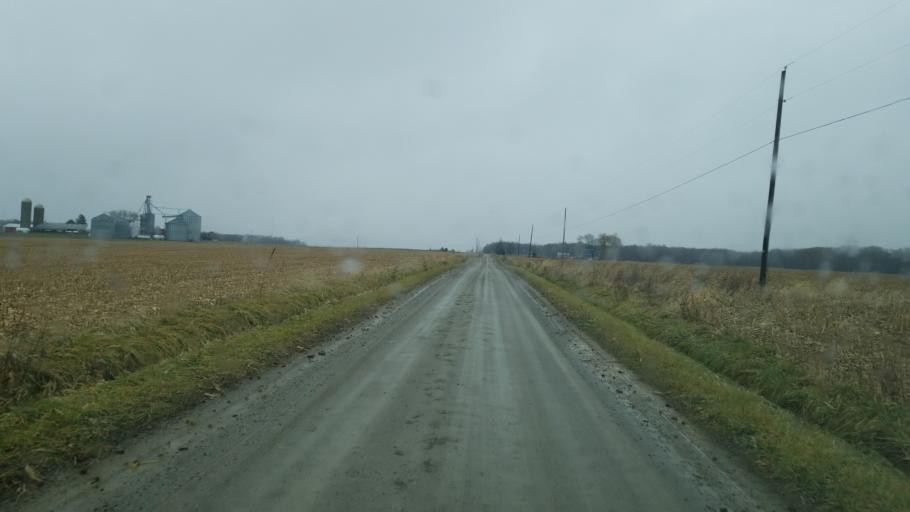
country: US
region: Ohio
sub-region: Ashtabula County
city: Roaming Shores
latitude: 41.5858
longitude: -80.7054
